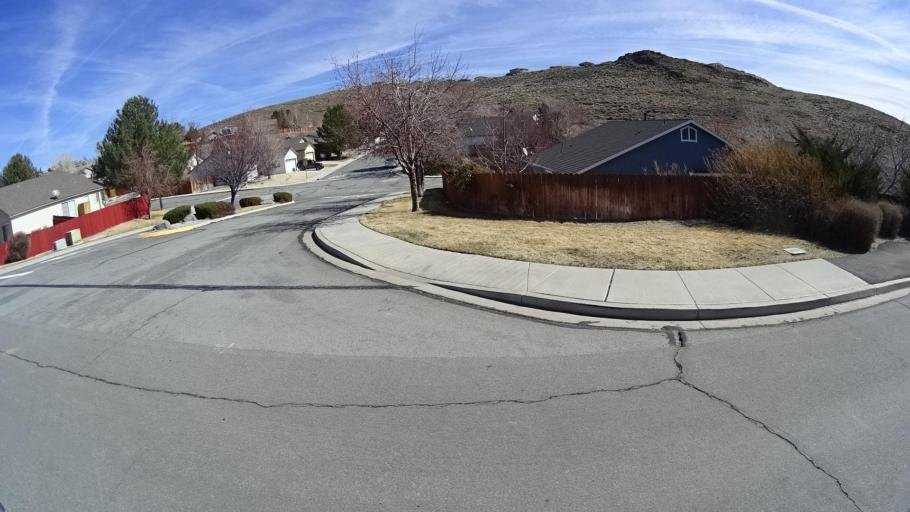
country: US
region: Nevada
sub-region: Washoe County
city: Sparks
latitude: 39.5770
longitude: -119.6979
